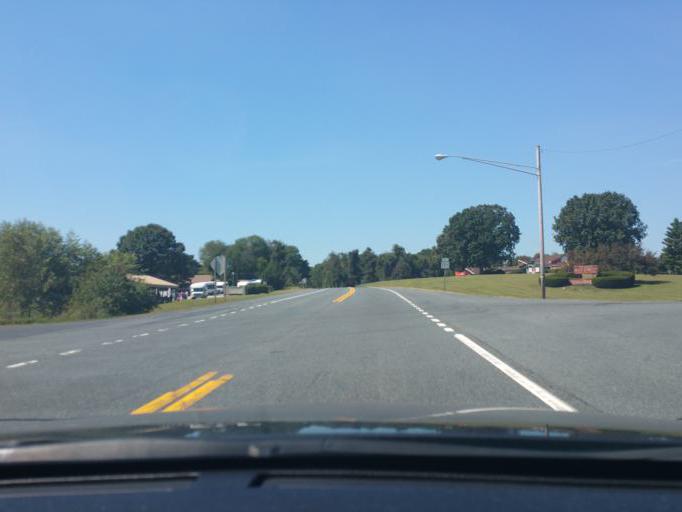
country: US
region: Maryland
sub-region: Harford County
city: Havre de Grace
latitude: 39.5750
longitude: -76.1483
